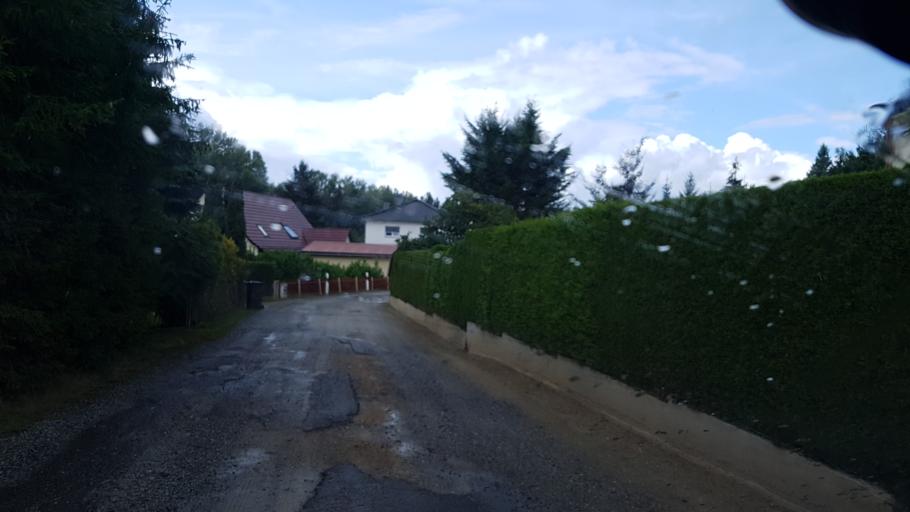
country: DE
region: Brandenburg
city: Tschernitz
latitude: 51.6059
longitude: 14.5946
